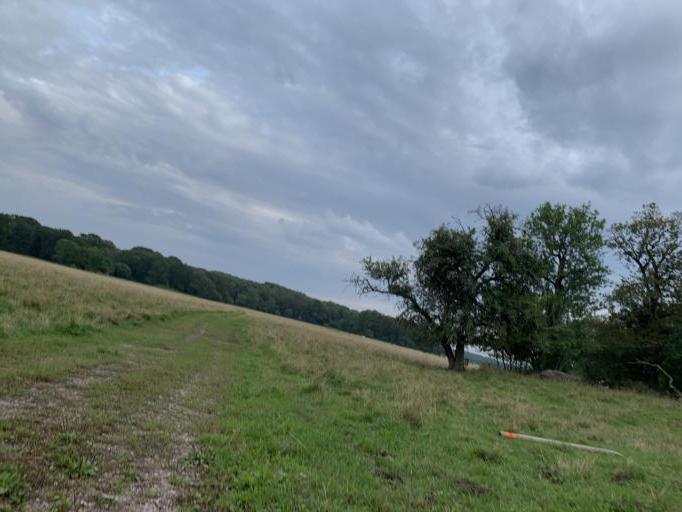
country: SE
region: Vaestmanland
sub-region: Hallstahammars Kommun
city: Kolback
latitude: 59.4812
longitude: 16.2169
